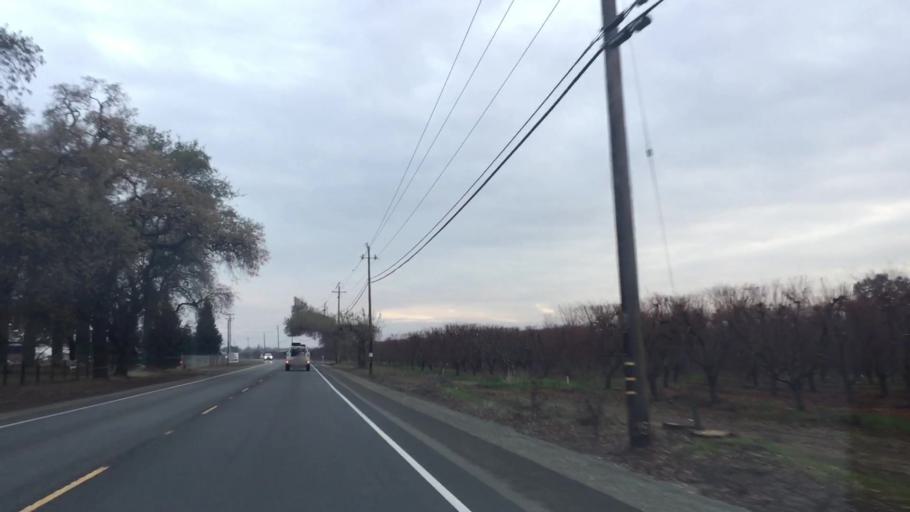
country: US
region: California
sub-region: Sutter County
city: Live Oak
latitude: 39.2852
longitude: -121.5946
